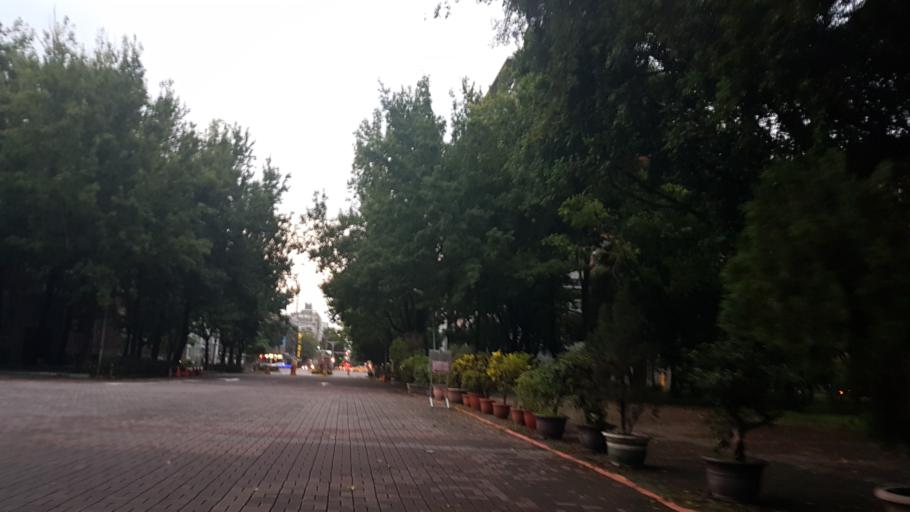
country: TW
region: Taipei
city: Taipei
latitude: 25.0196
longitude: 121.5434
